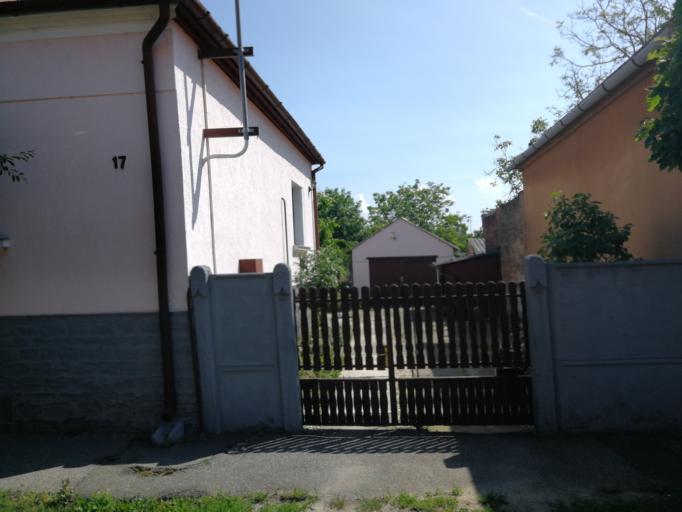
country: HU
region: Vas
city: Sarvar
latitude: 47.2524
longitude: 16.9211
